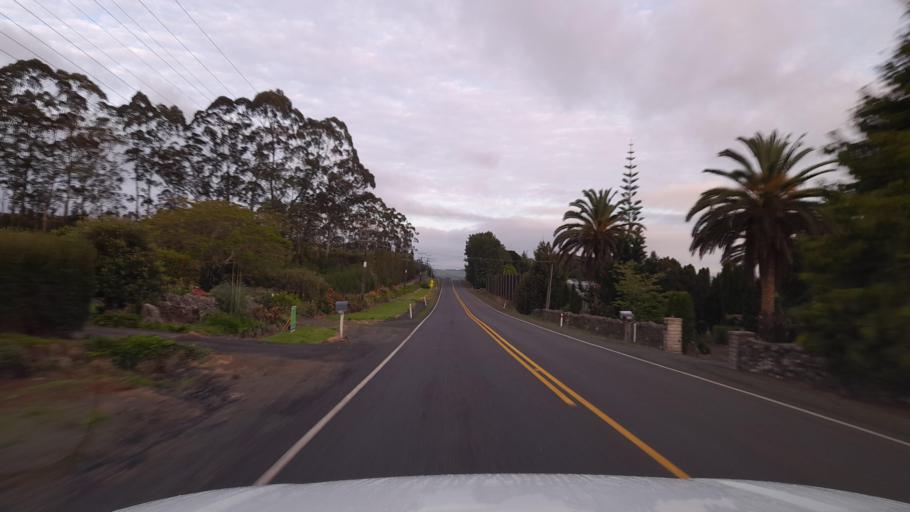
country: NZ
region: Northland
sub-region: Whangarei
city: Maungatapere
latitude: -35.7463
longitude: 174.1573
